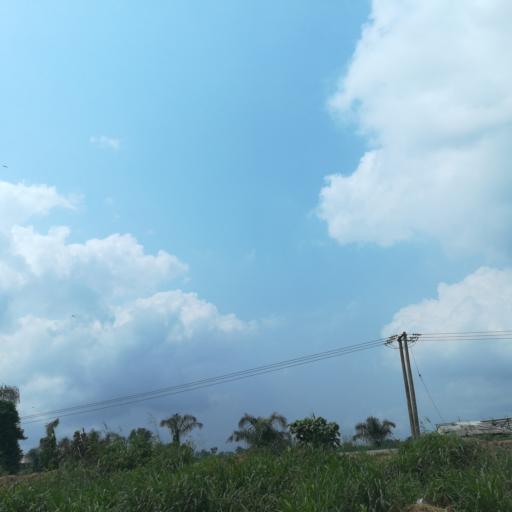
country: NG
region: Rivers
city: Okrika
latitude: 4.8079
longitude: 7.1006
